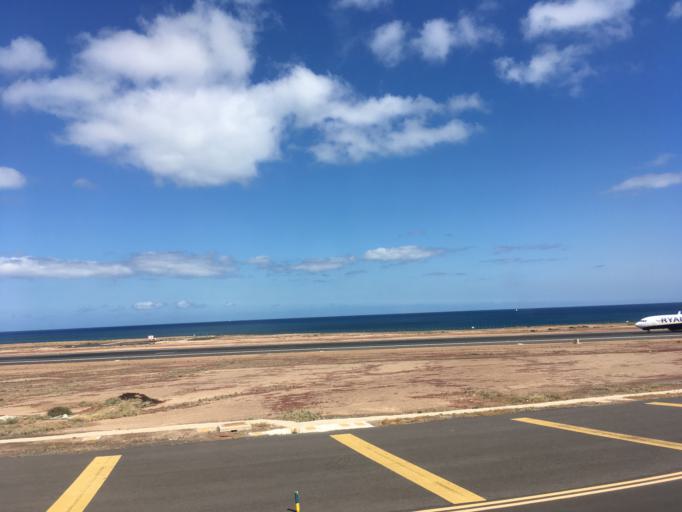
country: ES
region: Canary Islands
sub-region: Provincia de Las Palmas
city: Tias
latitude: 28.9478
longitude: -13.6059
